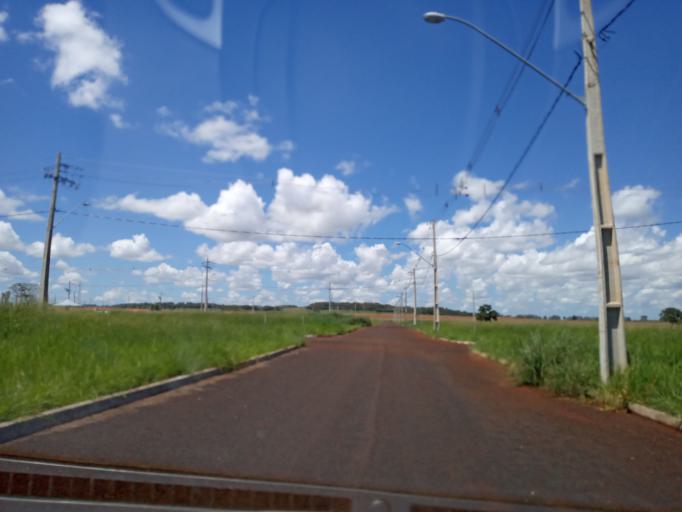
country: BR
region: Minas Gerais
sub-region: Centralina
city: Centralina
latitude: -18.5958
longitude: -49.1996
